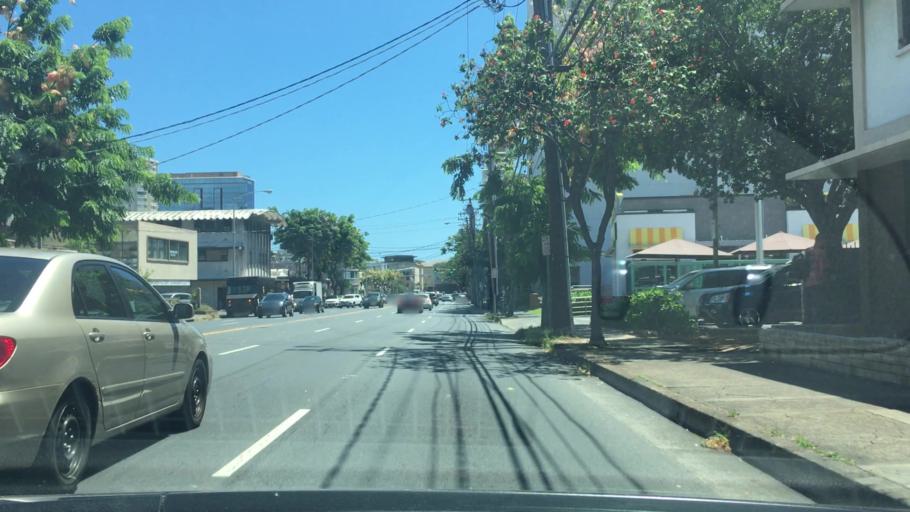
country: US
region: Hawaii
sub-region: Honolulu County
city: Honolulu
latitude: 21.2977
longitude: -157.8407
